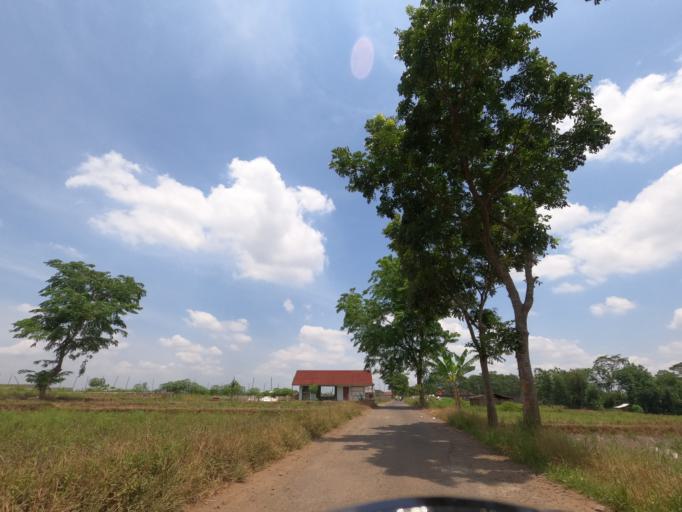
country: ID
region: West Java
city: Pamanukan
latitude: -6.5234
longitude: 107.7756
